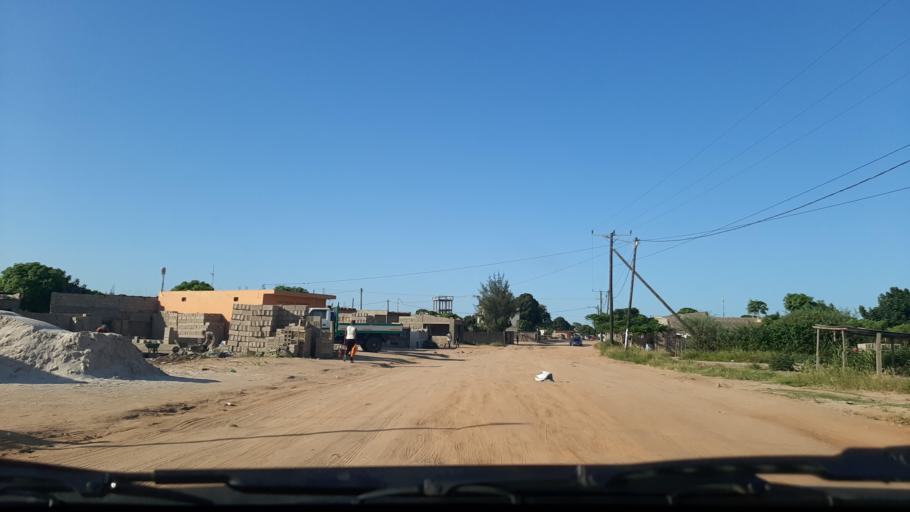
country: MZ
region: Maputo City
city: Maputo
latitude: -25.8029
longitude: 32.5475
